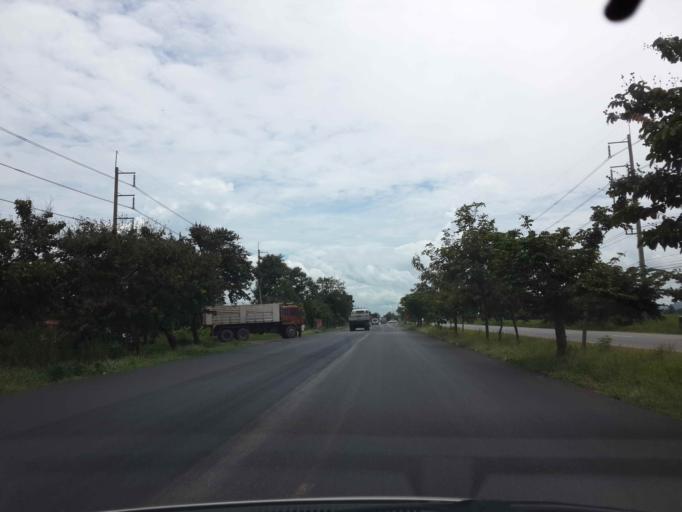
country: TH
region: Ratchaburi
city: Pak Tho
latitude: 13.4227
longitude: 99.8085
